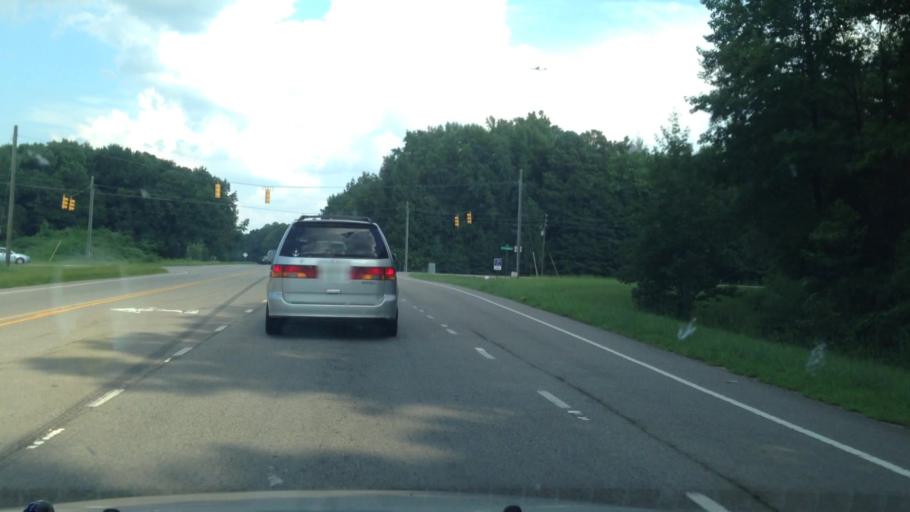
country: US
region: North Carolina
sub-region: Lee County
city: Broadway
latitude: 35.4412
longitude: -79.0999
